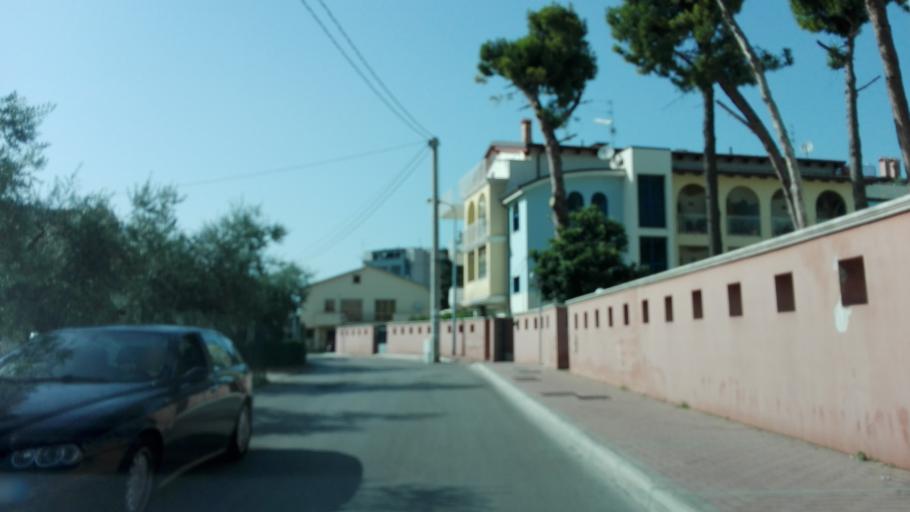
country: IT
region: Abruzzo
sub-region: Provincia di Pescara
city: Montesilvano Marina
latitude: 42.5094
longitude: 14.1392
